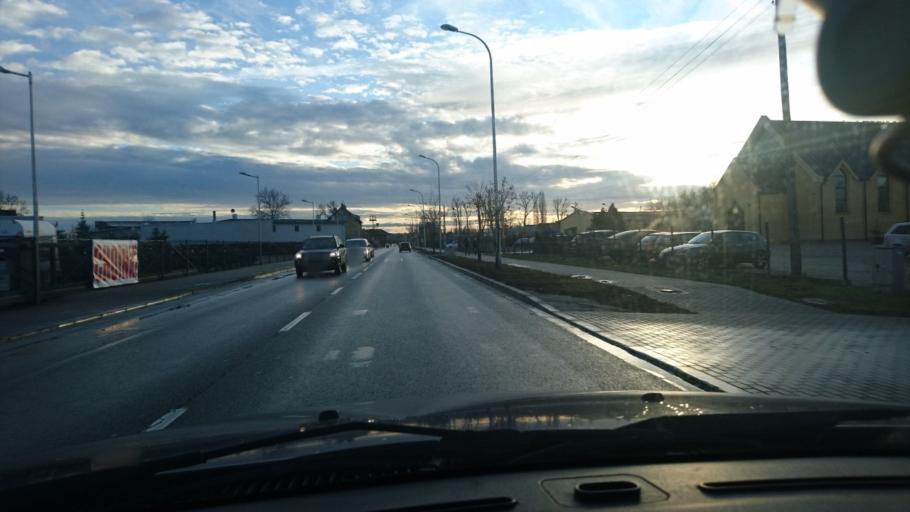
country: PL
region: Greater Poland Voivodeship
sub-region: Powiat kepinski
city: Kepno
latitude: 51.2926
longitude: 17.9951
